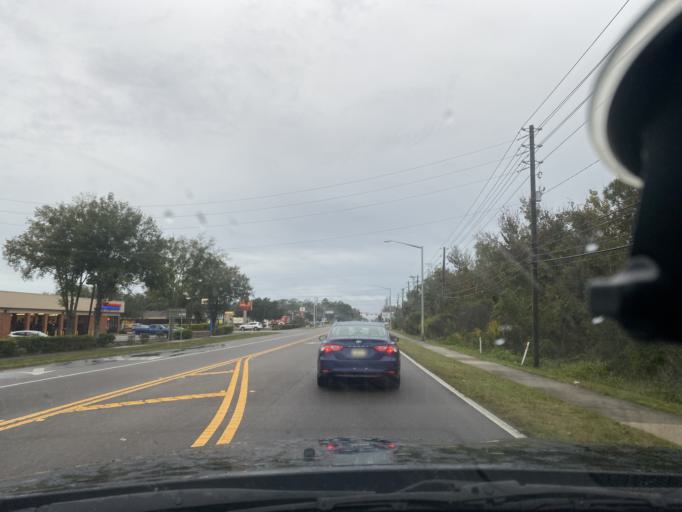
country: US
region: Florida
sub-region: Orange County
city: Azalea Park
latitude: 28.5392
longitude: -81.2731
